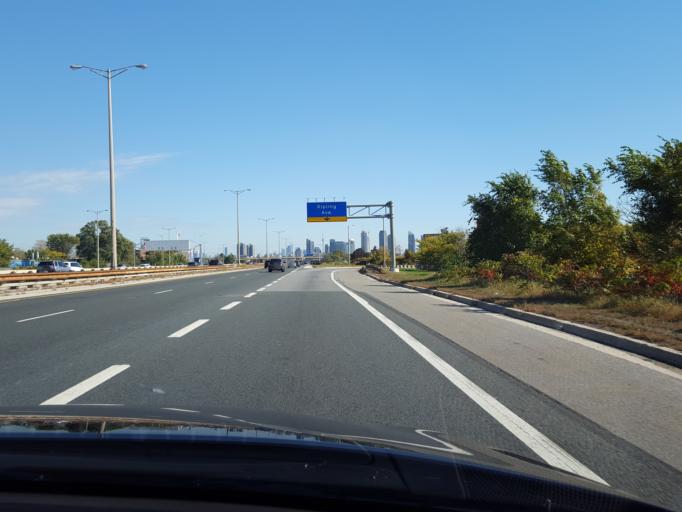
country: CA
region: Ontario
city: Etobicoke
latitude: 43.6184
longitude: -79.5219
